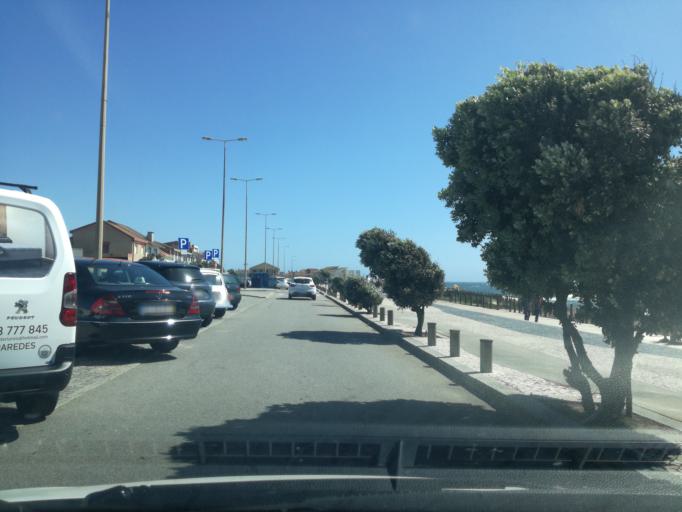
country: PT
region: Porto
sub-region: Matosinhos
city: Lavra
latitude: 41.2682
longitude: -8.7263
